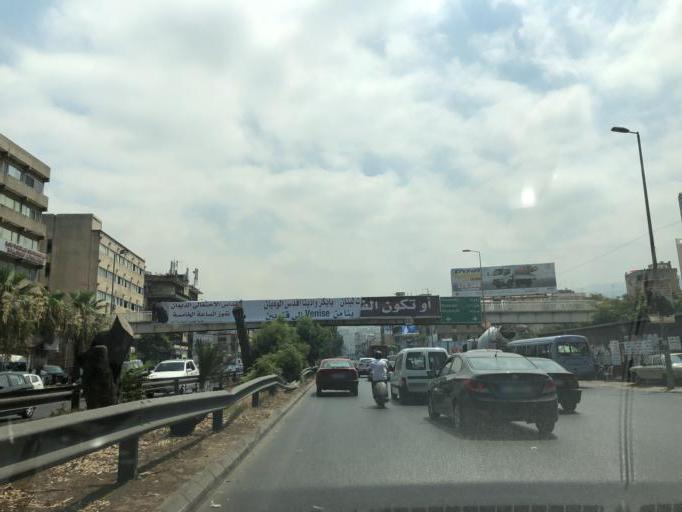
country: LB
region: Mont-Liban
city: Jdaidet el Matn
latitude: 33.8949
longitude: 35.5575
